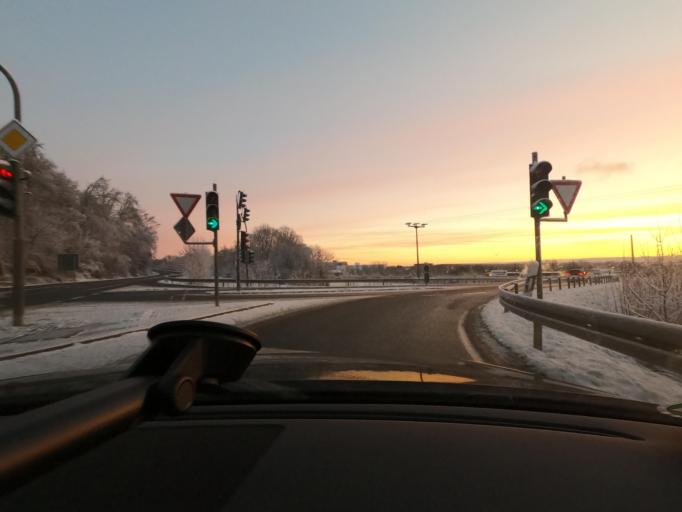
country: DE
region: Thuringia
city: Leinefelde
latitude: 51.3743
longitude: 10.3128
